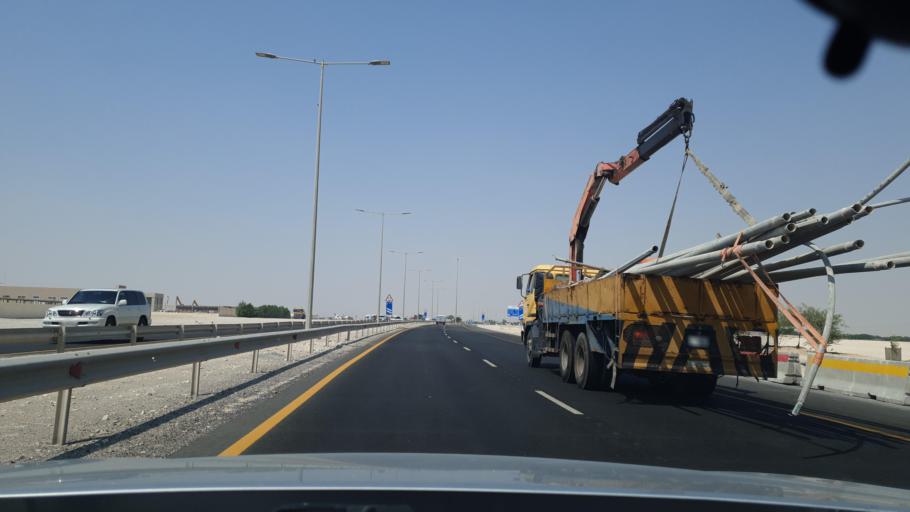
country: QA
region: Al Khawr
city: Al Khawr
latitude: 25.7194
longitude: 51.5020
